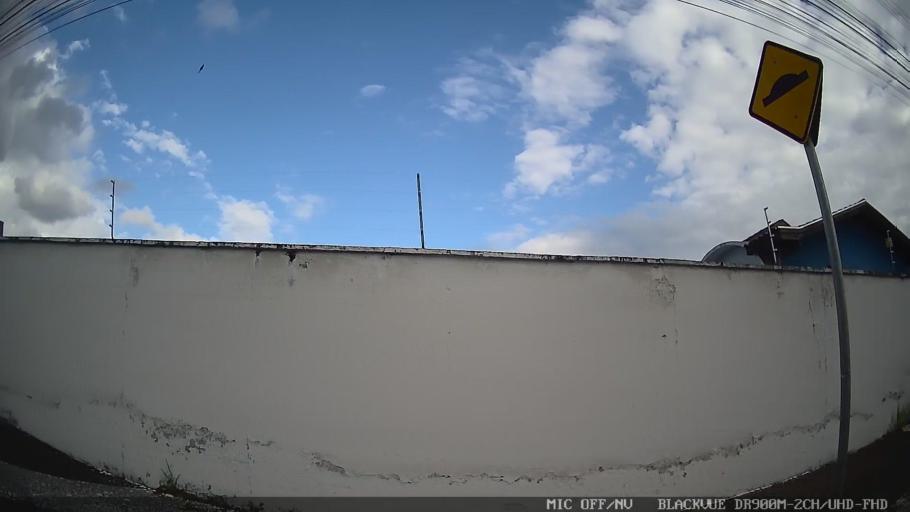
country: BR
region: Sao Paulo
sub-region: Caraguatatuba
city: Caraguatatuba
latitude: -23.6280
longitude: -45.4268
